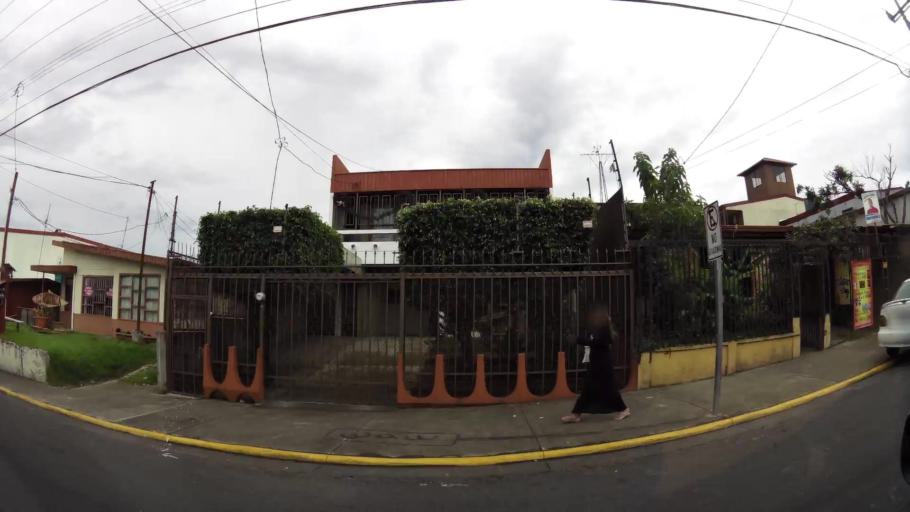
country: CR
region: San Jose
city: Ipis
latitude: 9.9759
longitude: -84.0095
